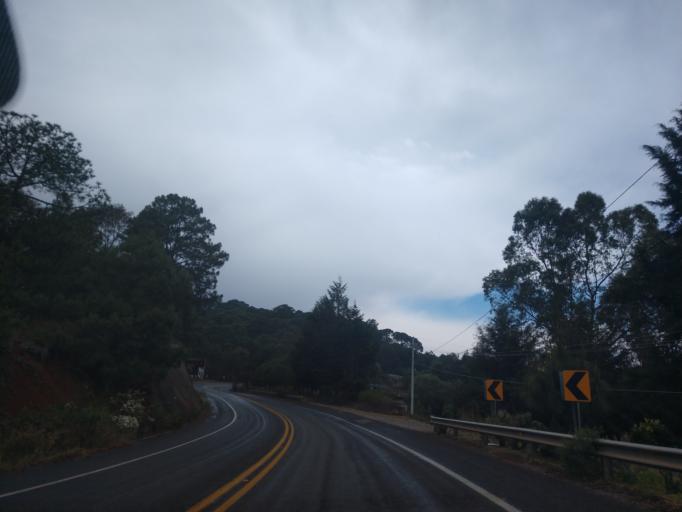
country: MX
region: Jalisco
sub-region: Mazamitla
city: Mazamitla
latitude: 19.9419
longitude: -103.0618
